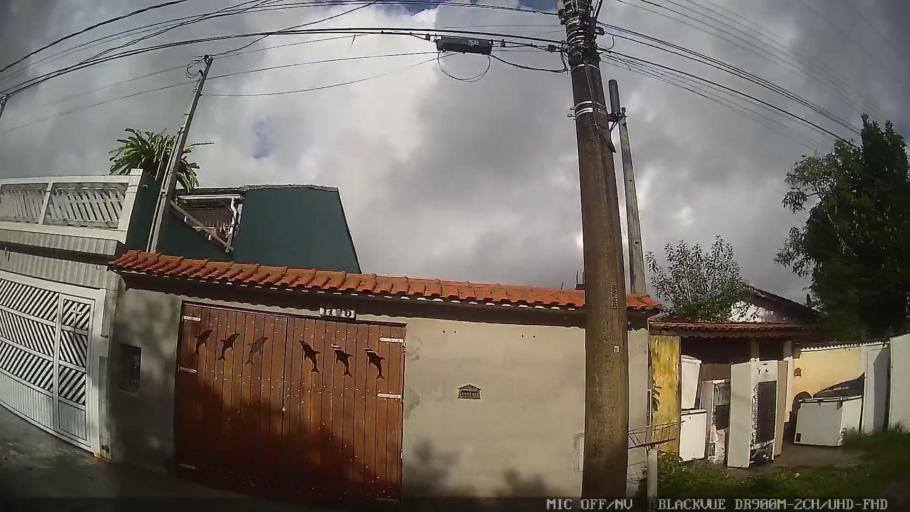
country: BR
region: Sao Paulo
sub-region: Itanhaem
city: Itanhaem
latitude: -24.2253
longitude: -46.8904
